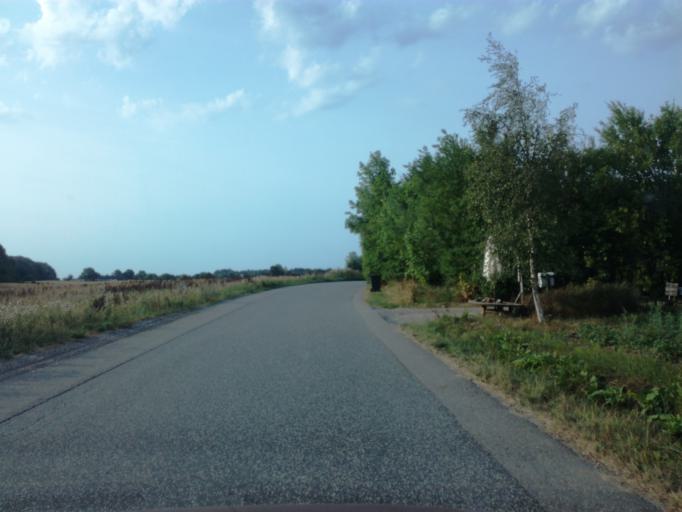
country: DK
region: South Denmark
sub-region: Vejle Kommune
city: Vejle
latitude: 55.6583
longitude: 9.5465
